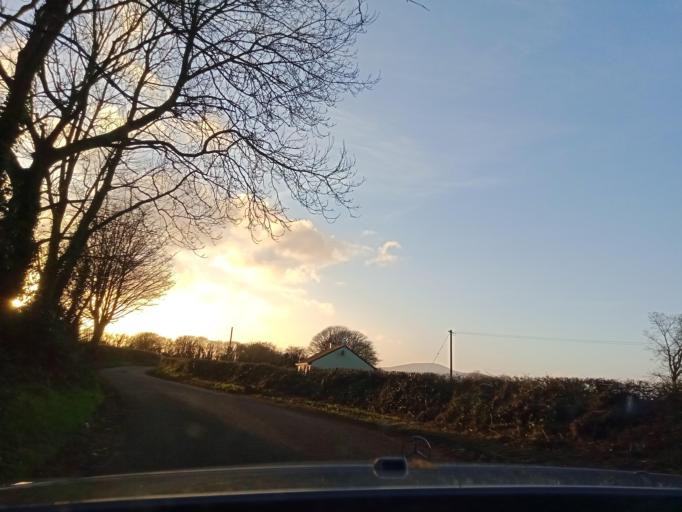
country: IE
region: Munster
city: Carrick-on-Suir
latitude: 52.4380
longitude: -7.3868
